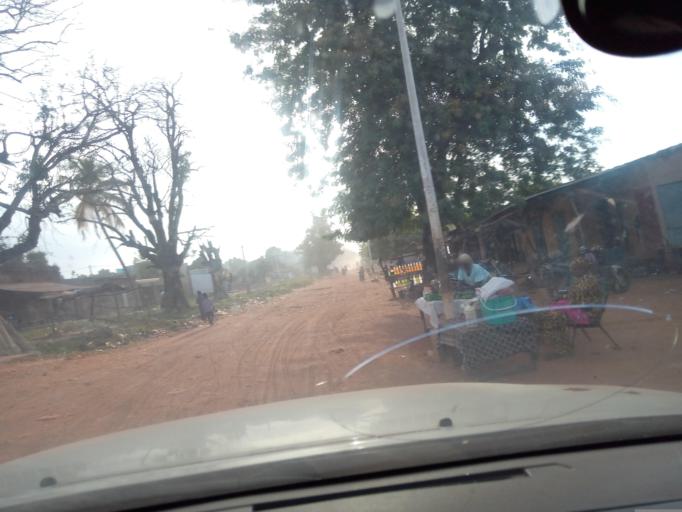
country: ML
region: Sikasso
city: Sikasso
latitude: 11.3142
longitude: -5.6477
